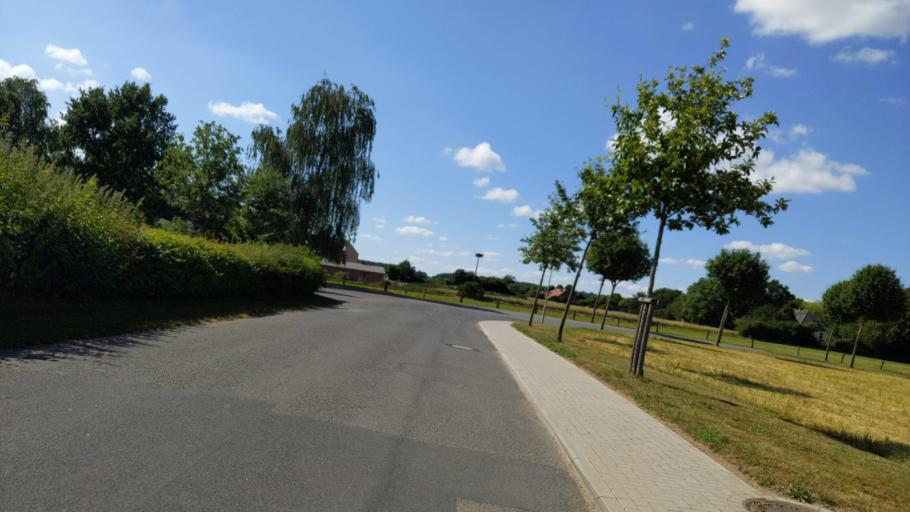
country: DE
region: Schleswig-Holstein
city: Kulpin
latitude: 53.7115
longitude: 10.6969
